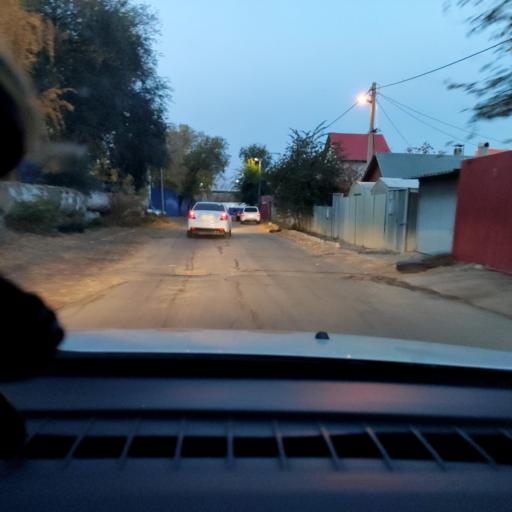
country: RU
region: Samara
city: Samara
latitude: 53.1890
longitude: 50.1708
